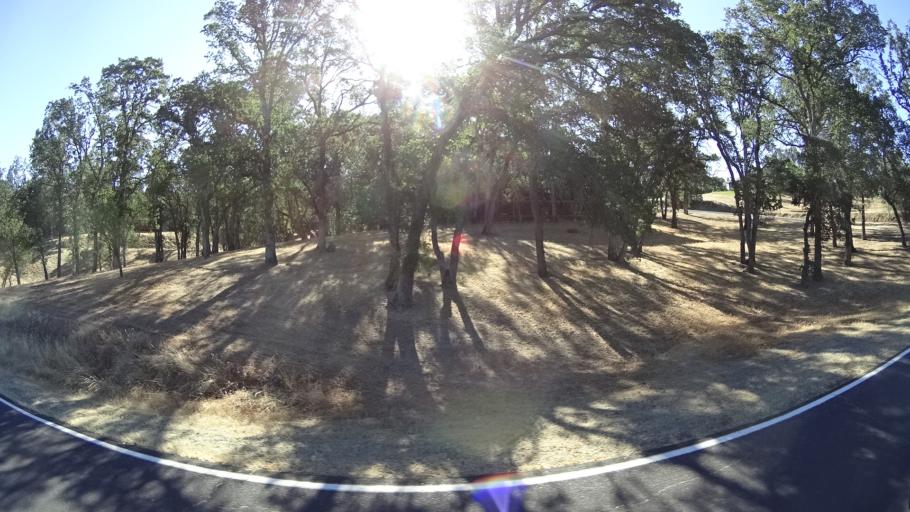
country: US
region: California
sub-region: Calaveras County
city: Rancho Calaveras
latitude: 38.1258
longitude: -120.8736
